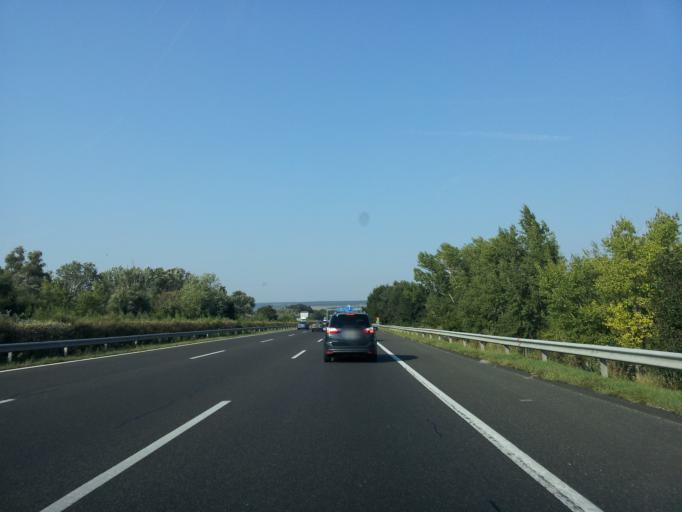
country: HU
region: Pest
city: Tarnok
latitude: 47.3714
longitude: 18.8281
